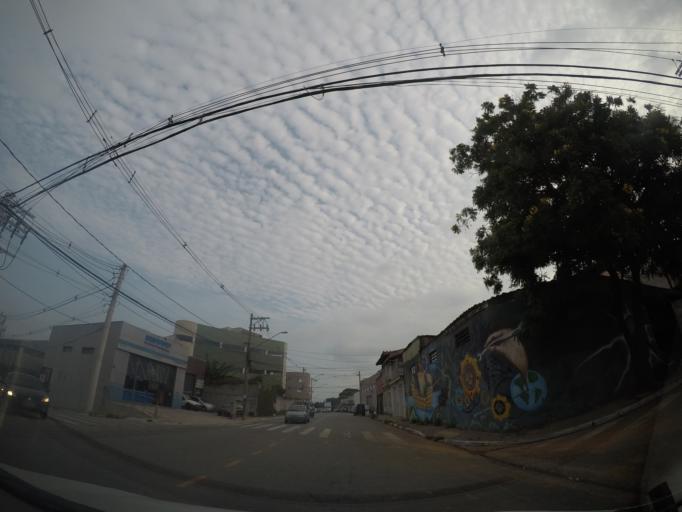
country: BR
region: Sao Paulo
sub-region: Guarulhos
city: Guarulhos
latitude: -23.4346
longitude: -46.5086
